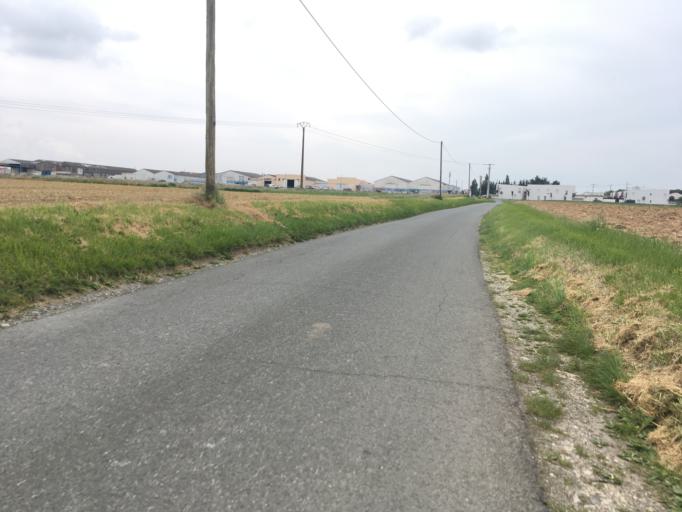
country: FR
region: Poitou-Charentes
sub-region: Departement de la Charente-Maritime
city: Aytre
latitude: 46.1439
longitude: -1.1214
